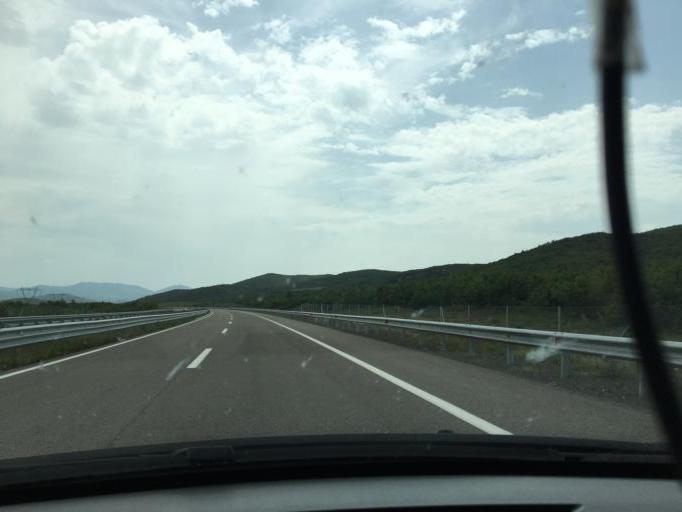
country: MK
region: Gevgelija
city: Miravci
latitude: 41.2873
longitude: 22.4395
